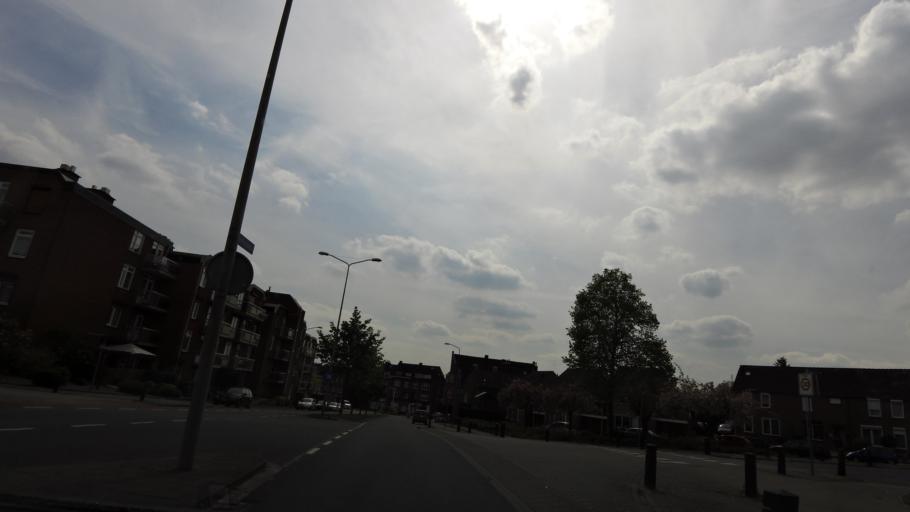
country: NL
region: Limburg
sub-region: Gemeente Heerlen
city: Nieuw-Lotbroek
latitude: 50.9153
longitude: 5.9603
